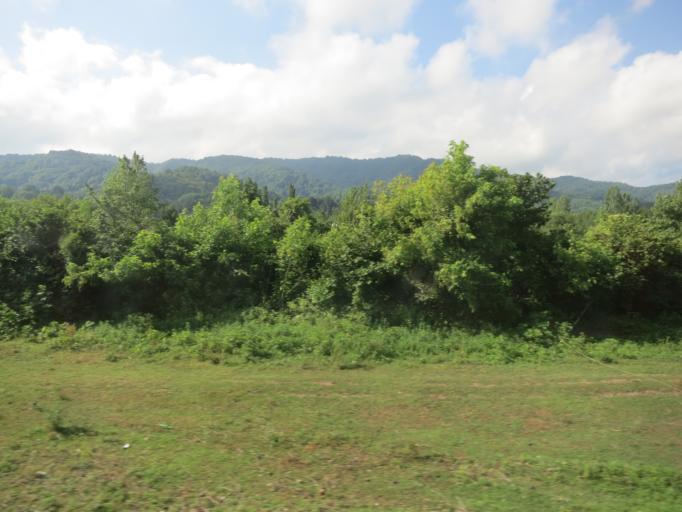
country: GE
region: Guria
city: Lanchkhuti
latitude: 42.0878
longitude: 42.1094
